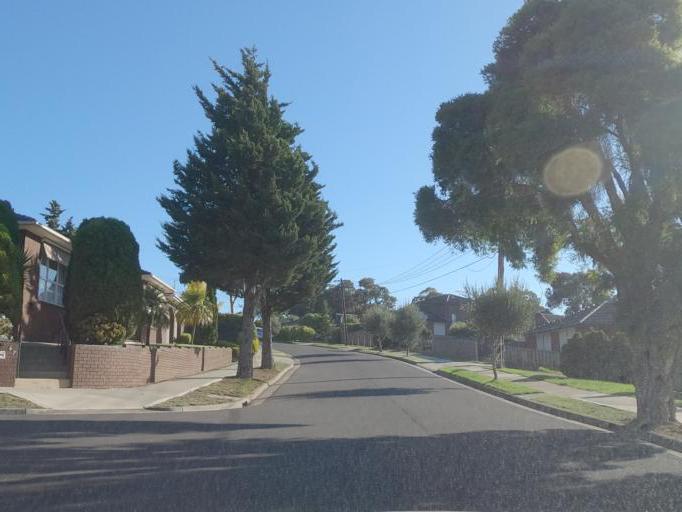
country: AU
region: Victoria
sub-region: Hume
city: Gladstone Park
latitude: -37.6828
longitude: 144.8972
